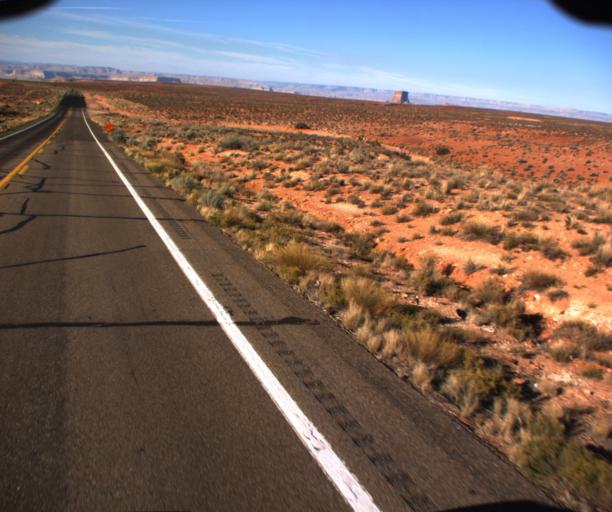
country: US
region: Arizona
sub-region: Coconino County
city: LeChee
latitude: 36.8704
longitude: -111.3415
